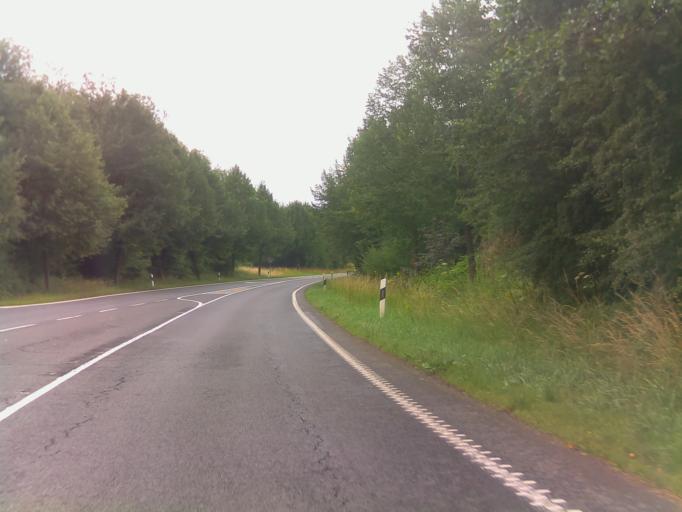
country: LU
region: Luxembourg
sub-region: Canton d'Esch-sur-Alzette
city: Reckange-sur-Mess
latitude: 49.5555
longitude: 6.0105
